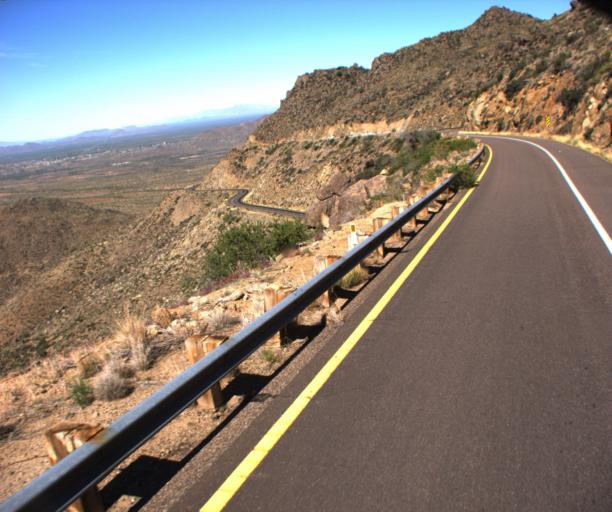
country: US
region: Arizona
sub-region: Yavapai County
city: Congress
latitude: 34.2037
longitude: -112.7695
